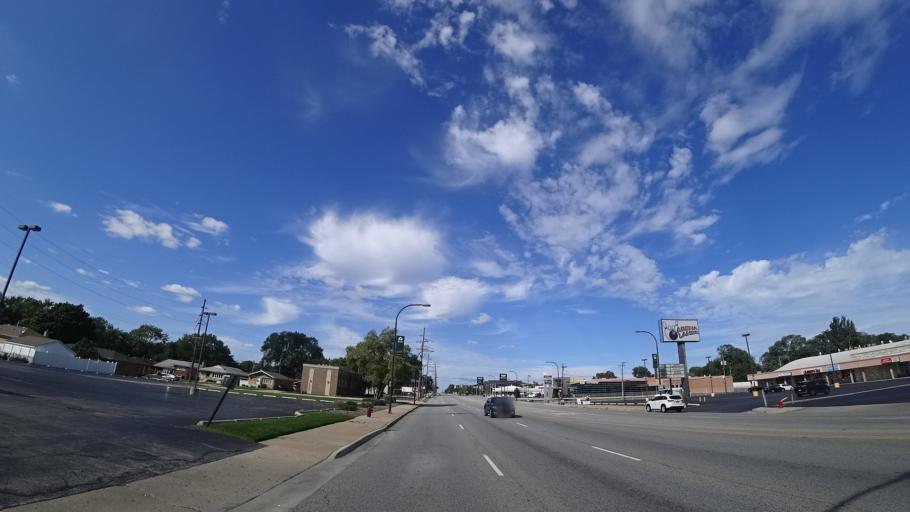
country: US
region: Illinois
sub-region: Cook County
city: Oak Lawn
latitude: 41.7062
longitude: -87.7404
